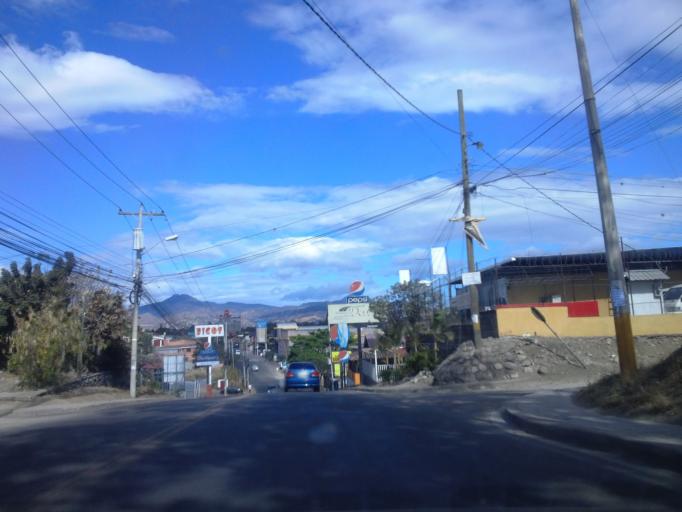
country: HN
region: Francisco Morazan
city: Tegucigalpa
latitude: 14.0533
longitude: -87.2266
